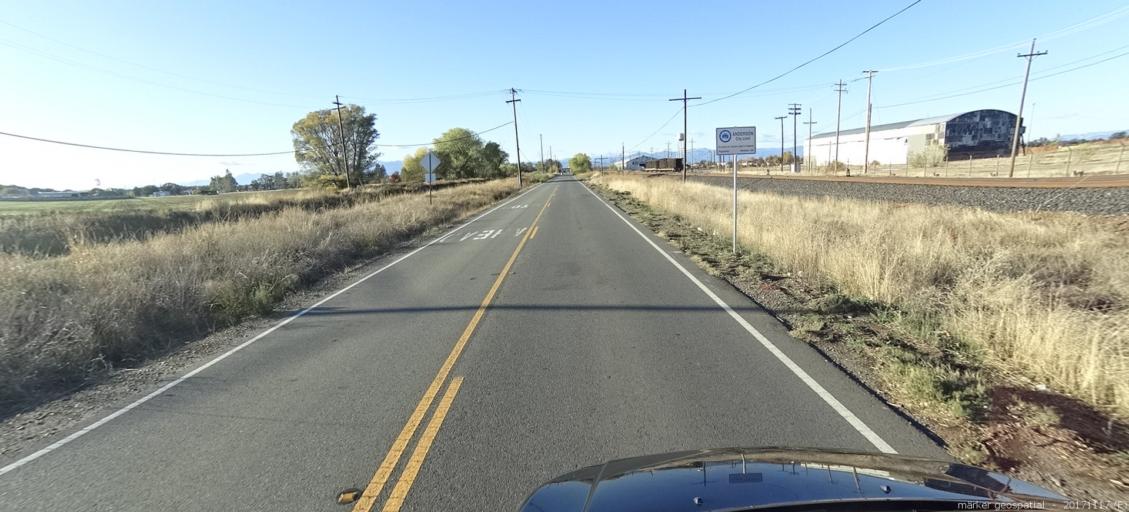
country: US
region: California
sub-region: Shasta County
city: Anderson
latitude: 40.4323
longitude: -122.2747
